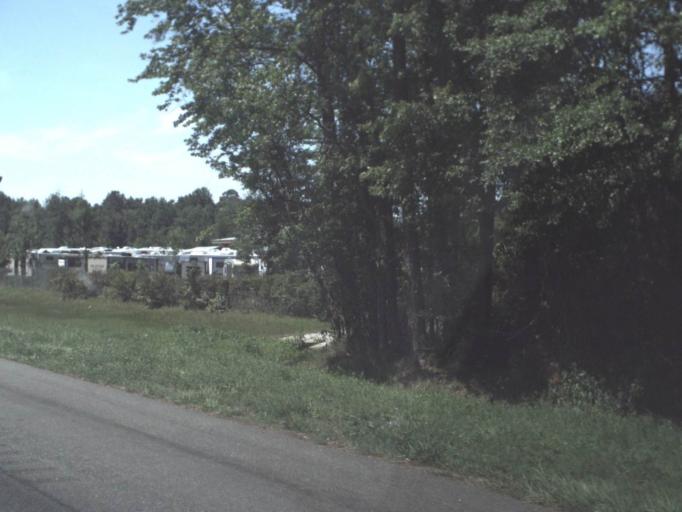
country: US
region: Florida
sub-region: Clay County
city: Bellair-Meadowbrook Terrace
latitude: 30.2220
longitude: -81.7625
